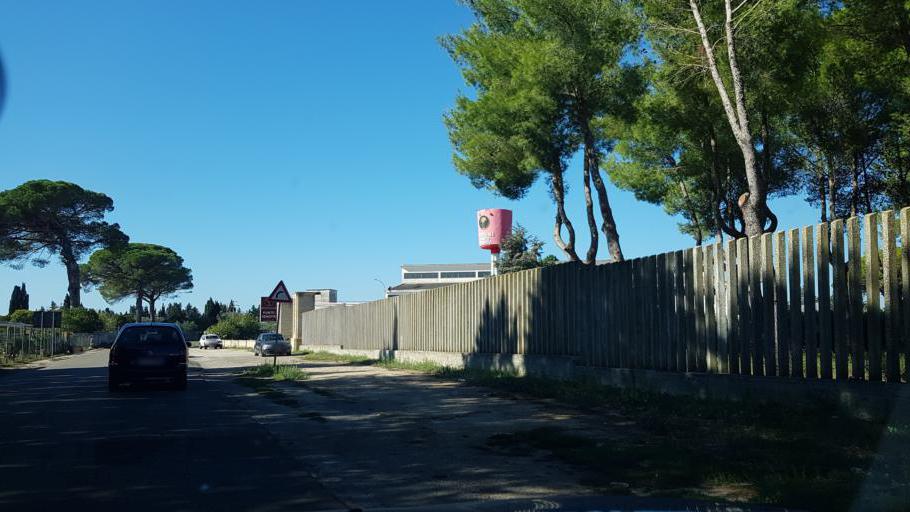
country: IT
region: Apulia
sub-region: Provincia di Lecce
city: Arnesano
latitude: 40.3352
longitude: 18.1019
